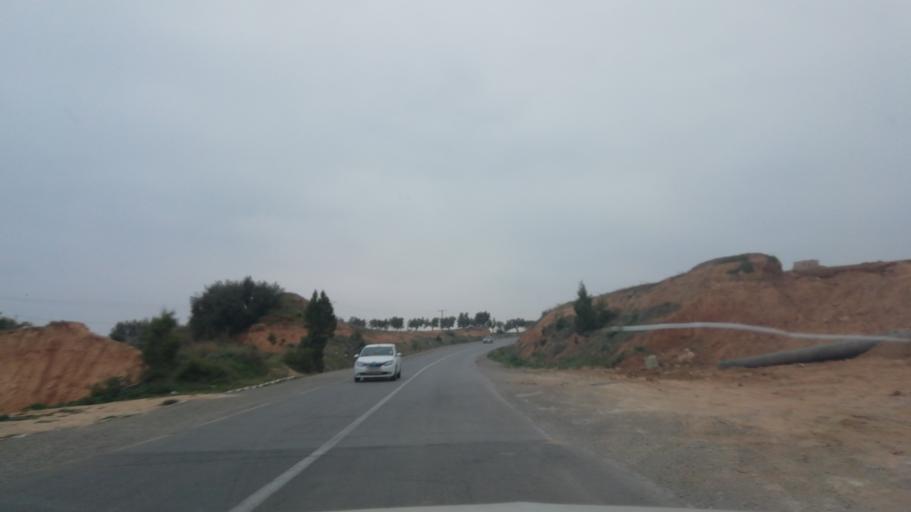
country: DZ
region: Sidi Bel Abbes
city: Sfizef
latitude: 35.2736
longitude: -0.1555
